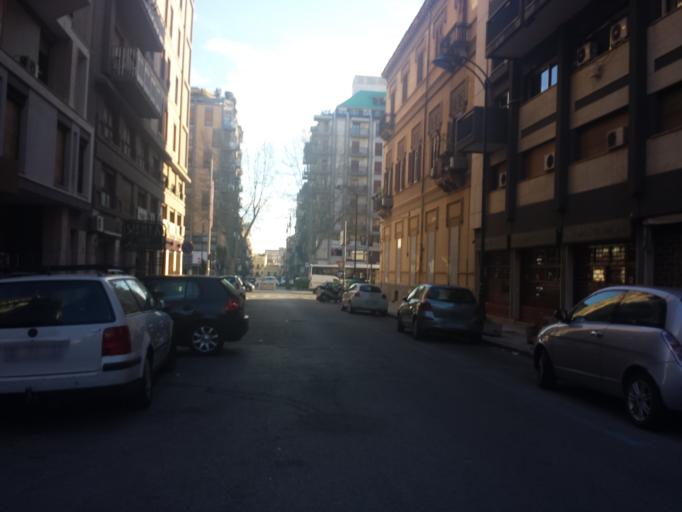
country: IT
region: Sicily
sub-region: Palermo
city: Palermo
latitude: 38.1273
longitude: 13.3529
